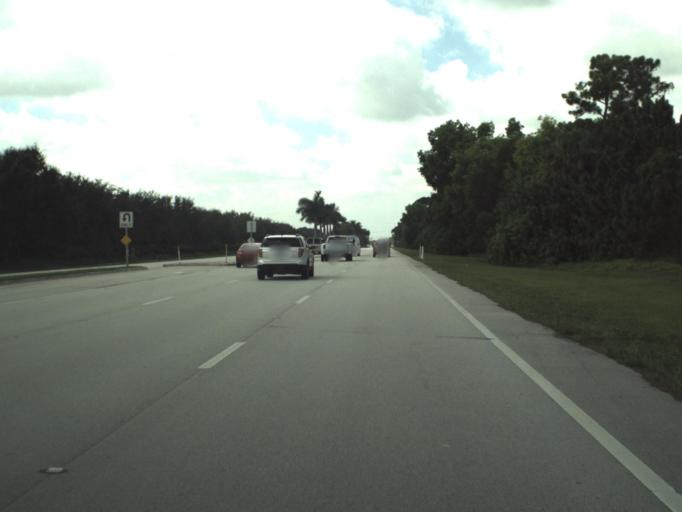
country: US
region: Florida
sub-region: Palm Beach County
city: Juno Beach
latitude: 26.8910
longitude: -80.0951
